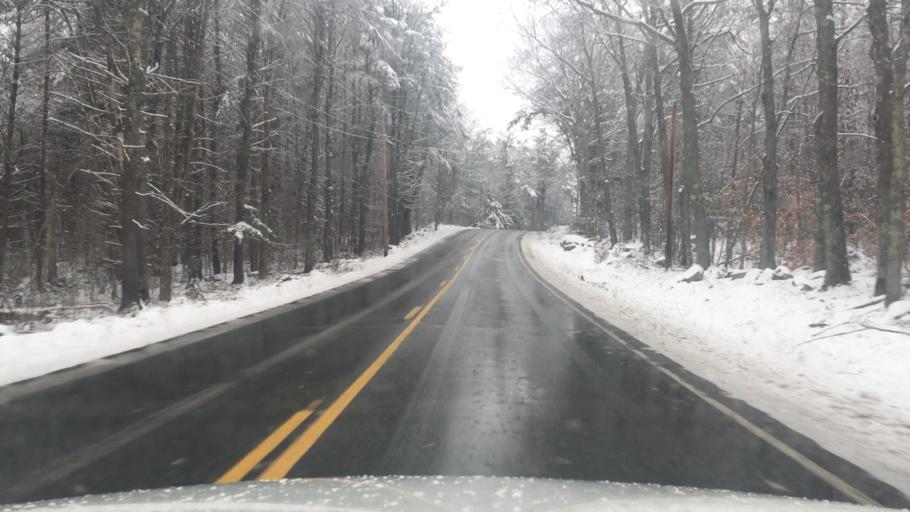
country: US
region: Maine
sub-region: Lincoln County
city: Jefferson
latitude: 44.2065
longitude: -69.4805
